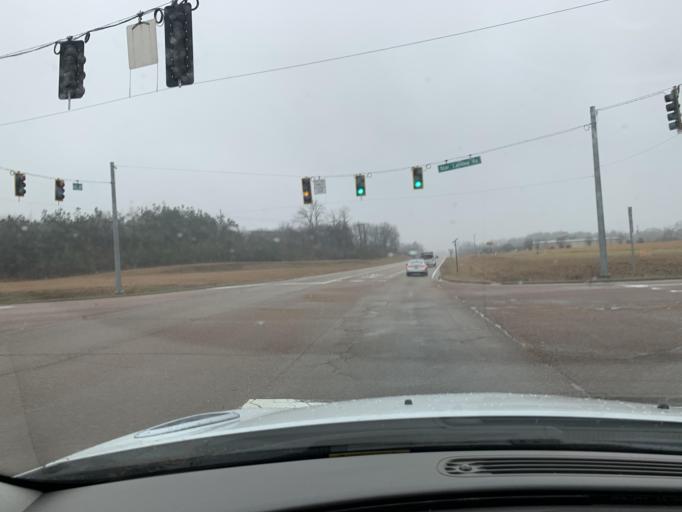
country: US
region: Mississippi
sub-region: De Soto County
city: Horn Lake
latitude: 34.9046
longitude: -89.9975
